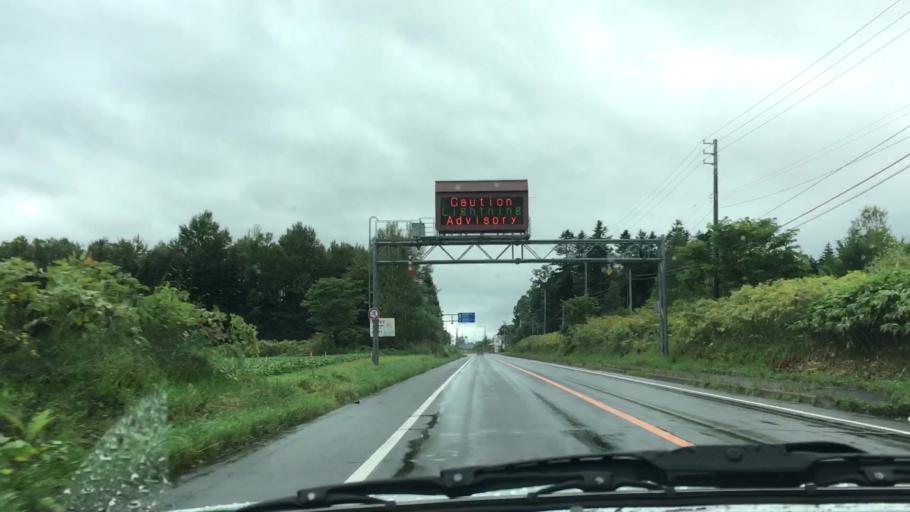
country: JP
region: Hokkaido
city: Niseko Town
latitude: 42.6969
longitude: 140.8427
